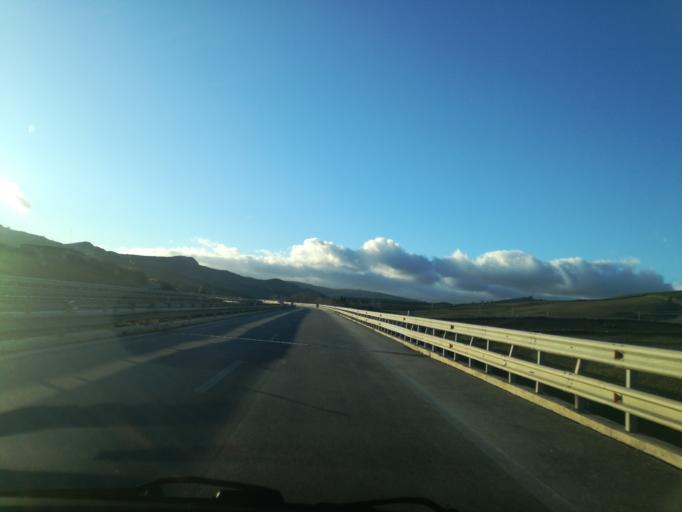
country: IT
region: Sicily
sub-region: Palermo
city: Castellana Sicula
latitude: 37.7437
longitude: 13.9898
